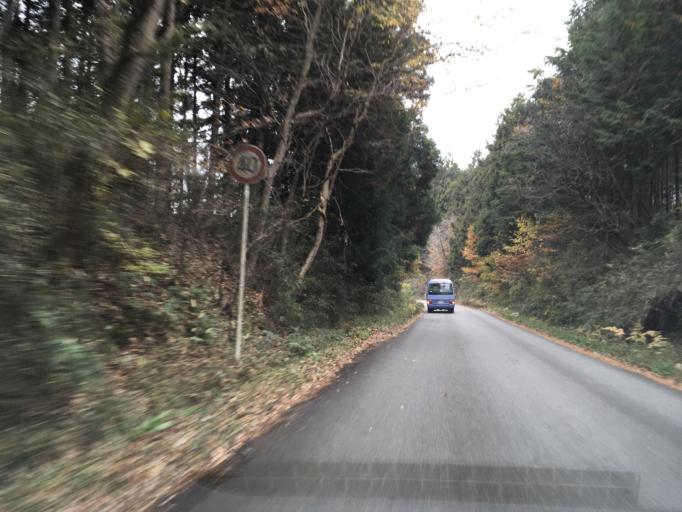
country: JP
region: Iwate
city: Ichinoseki
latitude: 38.8306
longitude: 141.0506
